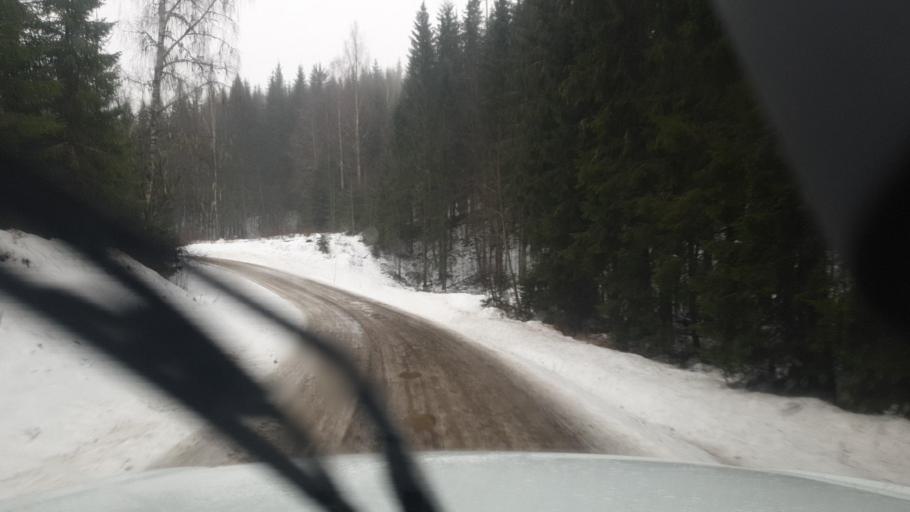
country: SE
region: Vaermland
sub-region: Eda Kommun
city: Charlottenberg
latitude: 60.0333
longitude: 12.5971
